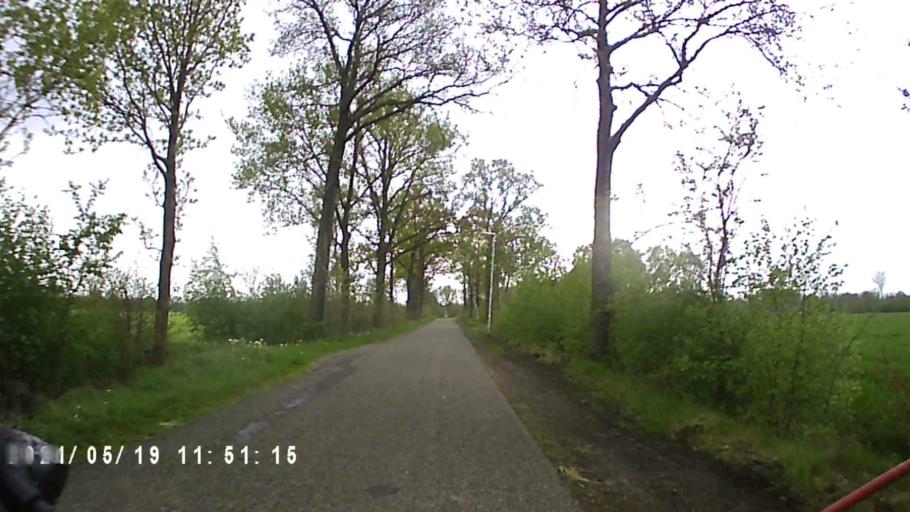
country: NL
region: Friesland
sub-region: Gemeente Kollumerland en Nieuwkruisland
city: Kollum
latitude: 53.2696
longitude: 6.1422
